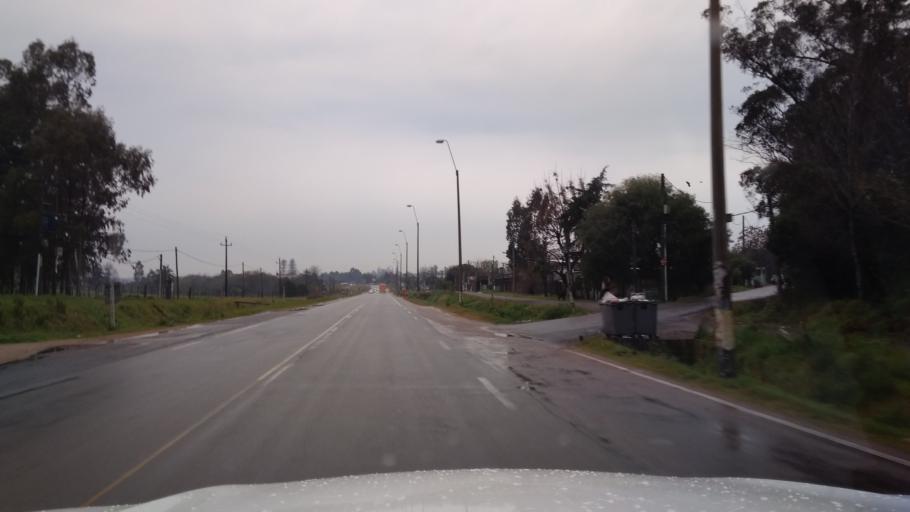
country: UY
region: Canelones
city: Toledo
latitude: -34.7598
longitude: -56.1147
